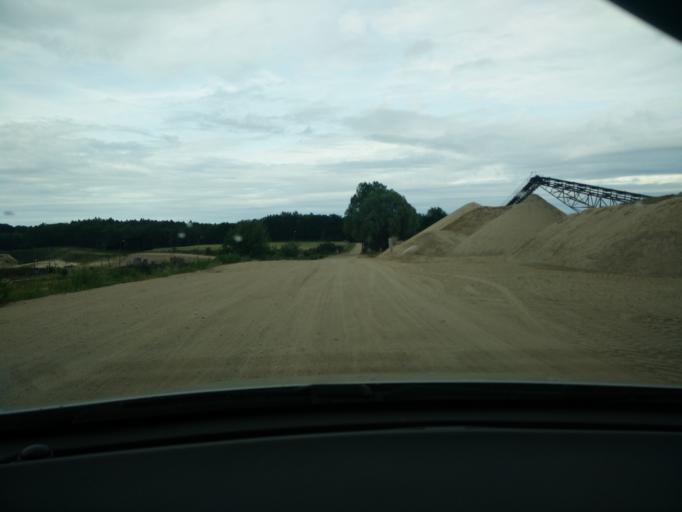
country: PL
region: Pomeranian Voivodeship
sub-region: Powiat pucki
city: Mrzezino
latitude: 54.6552
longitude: 18.4358
